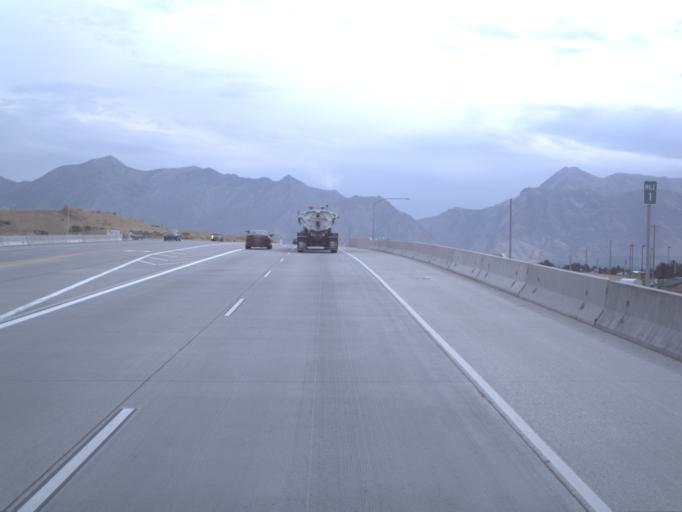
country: US
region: Utah
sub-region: Utah County
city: Lehi
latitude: 40.4320
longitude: -111.8750
